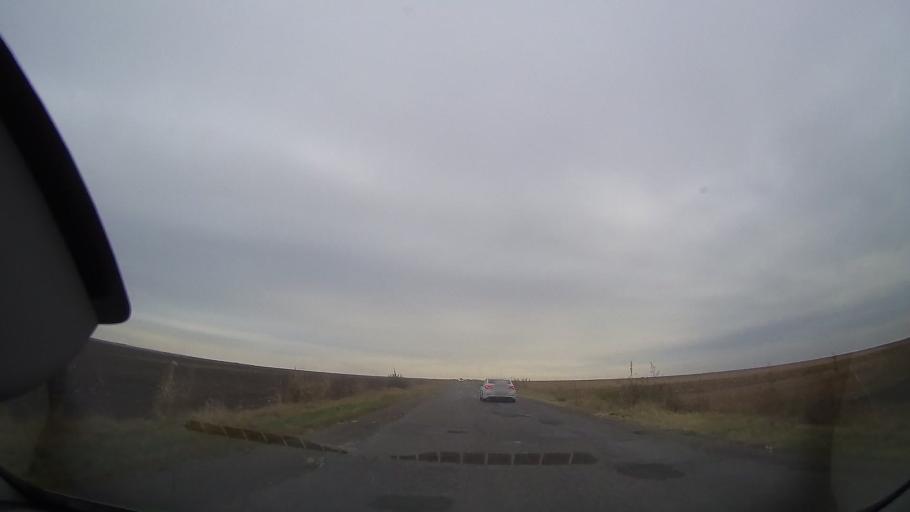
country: RO
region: Ialomita
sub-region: Oras Amara
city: Amara
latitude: 44.6671
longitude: 27.3007
